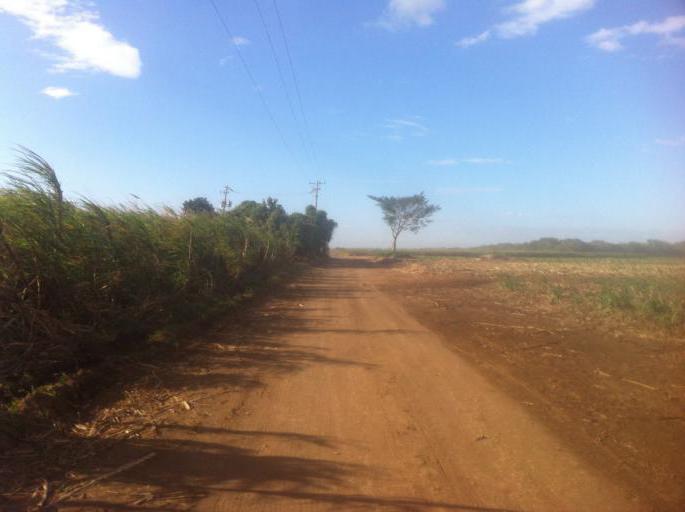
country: NI
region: Managua
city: Masachapa
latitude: 11.8591
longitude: -86.5534
